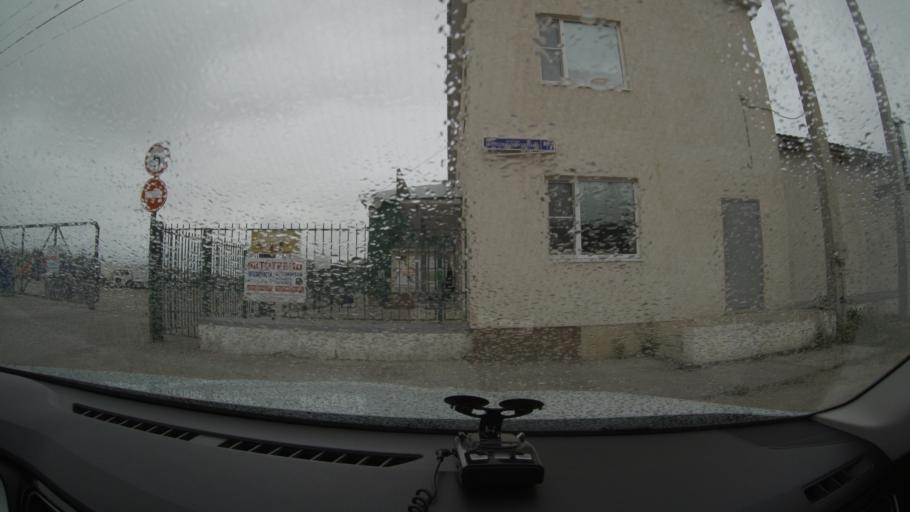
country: RU
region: Komi Republic
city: Kozhva
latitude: 65.1101
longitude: 57.0127
